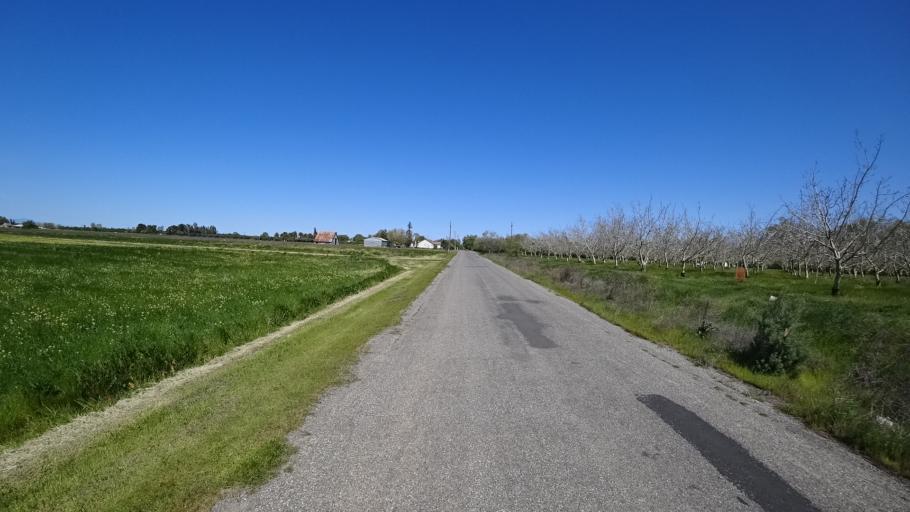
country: US
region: California
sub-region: Glenn County
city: Hamilton City
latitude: 39.7928
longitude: -122.0571
